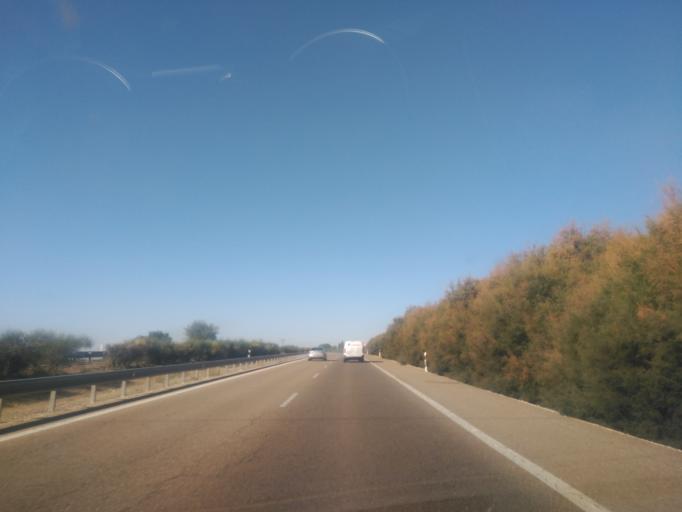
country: ES
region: Castille and Leon
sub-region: Provincia de Valladolid
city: Cisterniga
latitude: 41.5973
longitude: -4.6454
